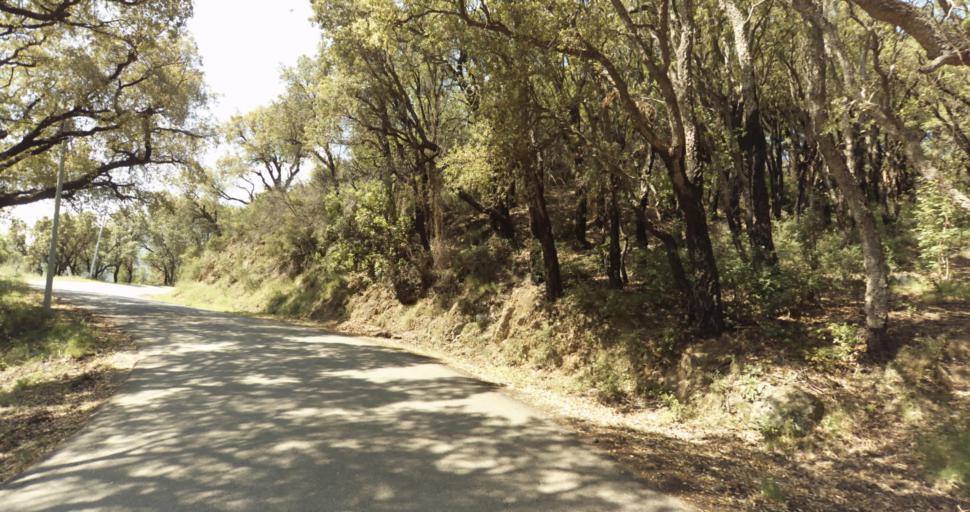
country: FR
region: Corsica
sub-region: Departement de la Haute-Corse
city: Biguglia
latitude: 42.6144
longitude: 9.4173
